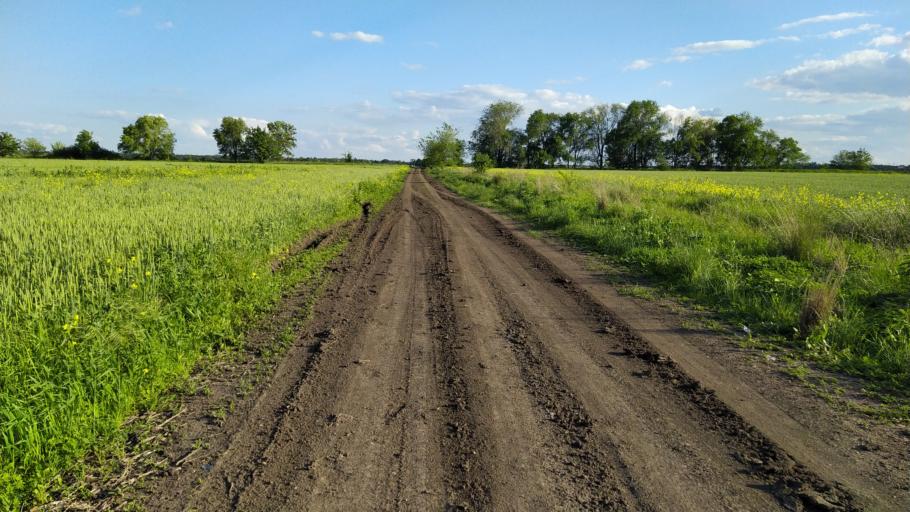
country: RU
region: Rostov
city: Bataysk
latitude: 47.1256
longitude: 39.7226
